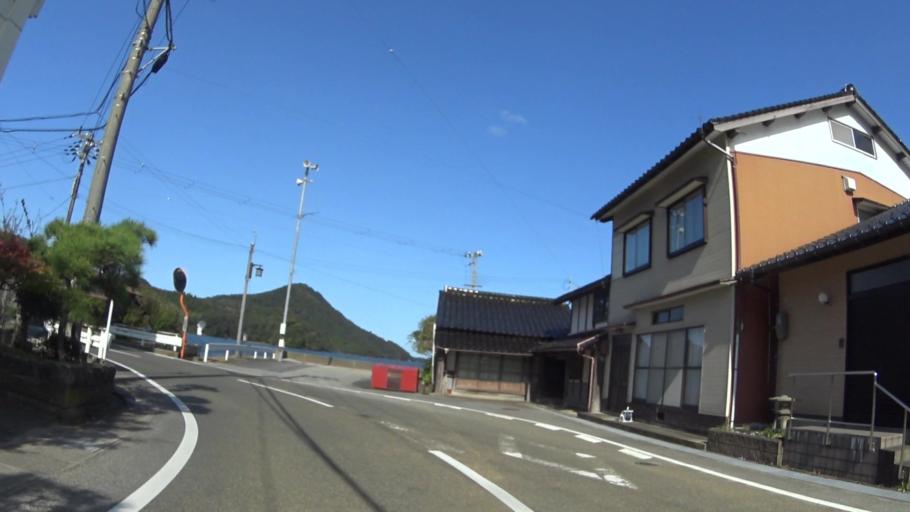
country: JP
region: Hyogo
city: Toyooka
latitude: 35.6076
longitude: 134.8936
